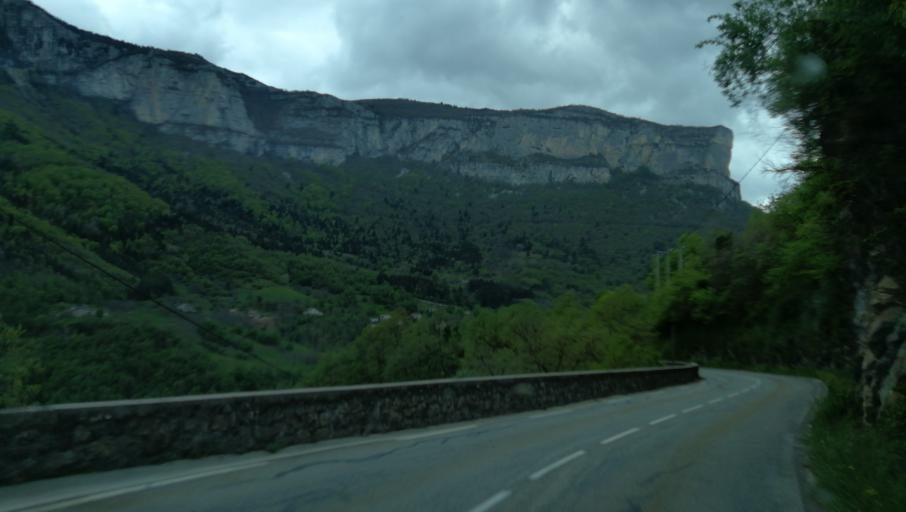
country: FR
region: Rhone-Alpes
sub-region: Departement de l'Isere
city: Pont-en-Royans
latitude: 45.0603
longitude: 5.4145
